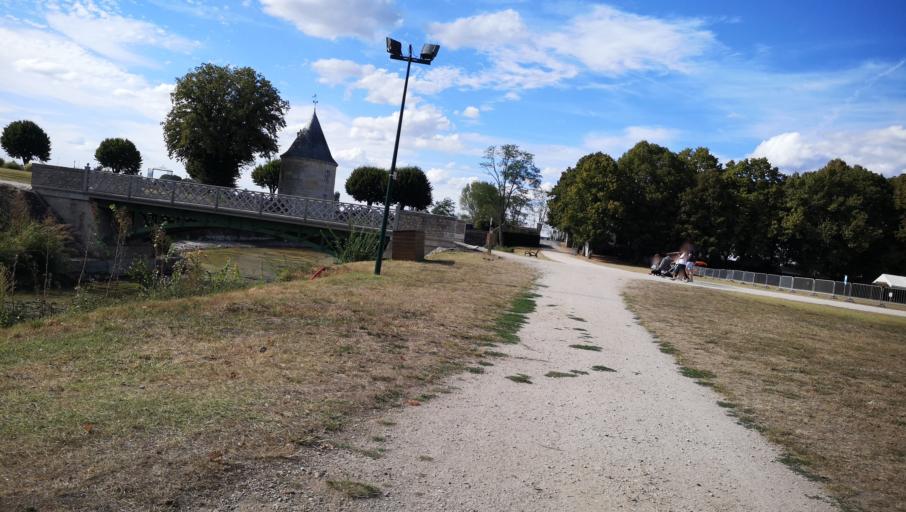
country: FR
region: Centre
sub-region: Departement du Loiret
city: Sully-sur-Loire
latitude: 47.7678
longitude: 2.3771
